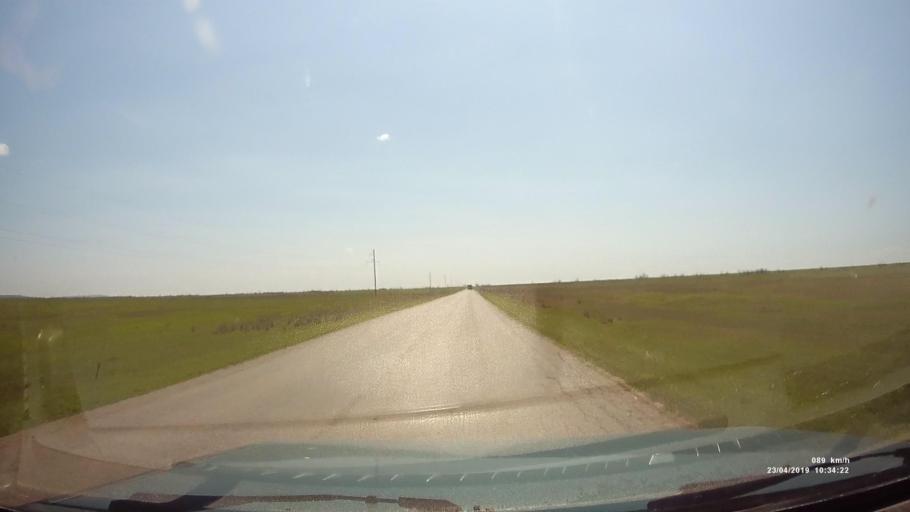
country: RU
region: Kalmykiya
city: Yashalta
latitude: 46.5647
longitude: 42.6094
